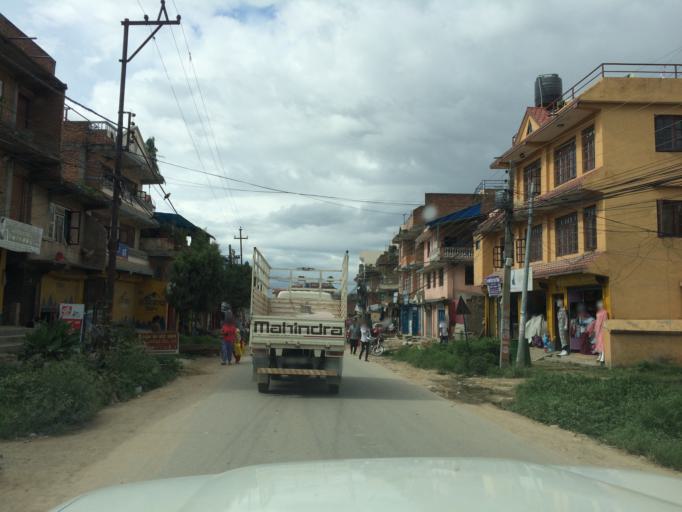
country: NP
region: Central Region
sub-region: Bagmati Zone
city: Patan
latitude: 27.6396
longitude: 85.3050
